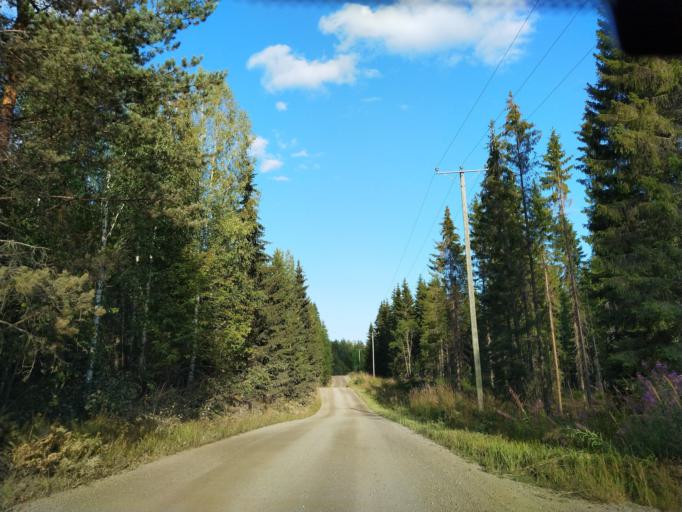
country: FI
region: Central Finland
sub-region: Jaemsae
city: Kuhmoinen
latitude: 61.6942
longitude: 24.9409
